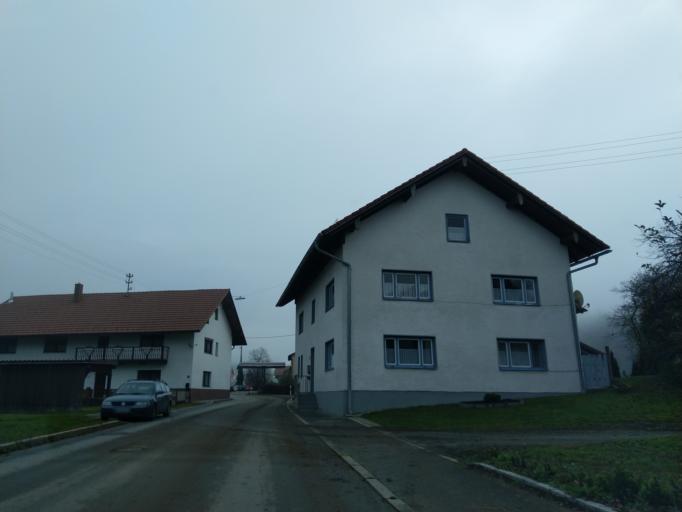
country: DE
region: Bavaria
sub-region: Lower Bavaria
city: Schollnach
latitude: 48.7751
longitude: 13.1894
